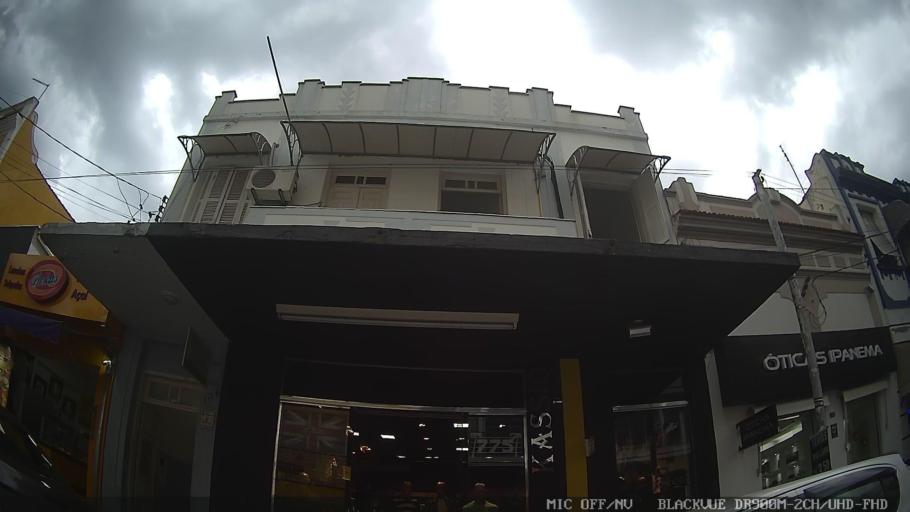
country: BR
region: Sao Paulo
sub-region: Amparo
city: Amparo
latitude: -22.7024
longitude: -46.7675
